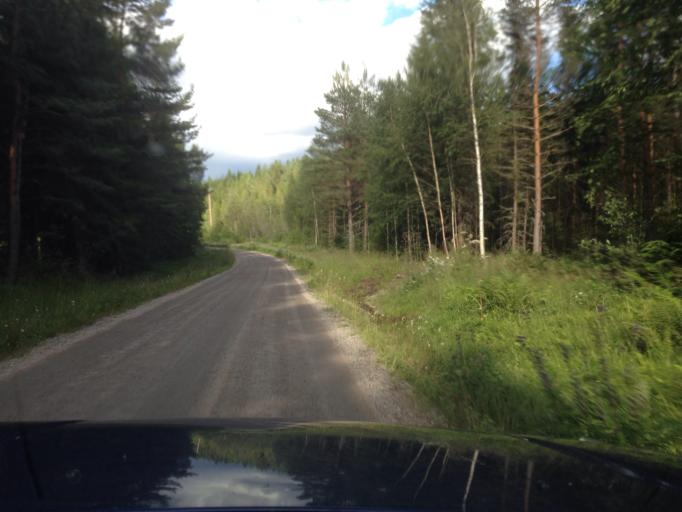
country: SE
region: Dalarna
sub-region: Ludvika Kommun
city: Abborrberget
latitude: 60.3072
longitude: 14.6478
